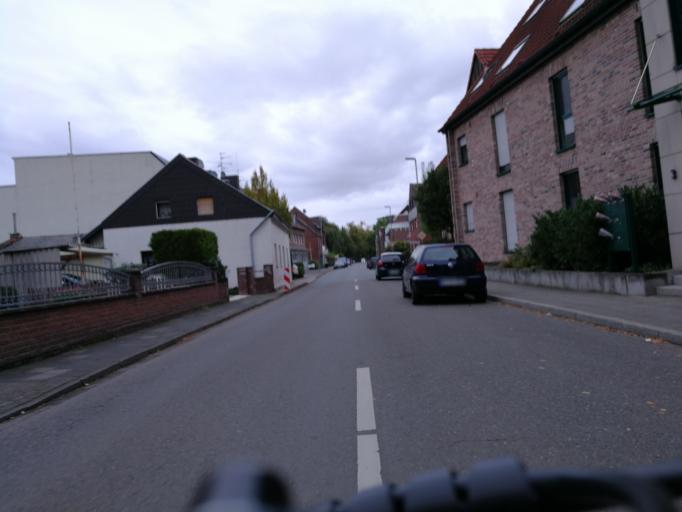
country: DE
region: North Rhine-Westphalia
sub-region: Regierungsbezirk Dusseldorf
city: Neuss
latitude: 51.1565
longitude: 6.7225
